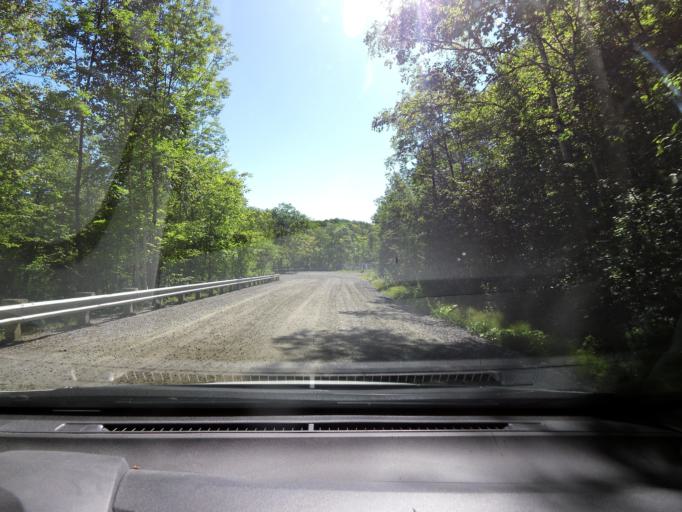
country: CA
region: Quebec
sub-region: Mauricie
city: Becancour
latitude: 46.5519
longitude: -72.4127
